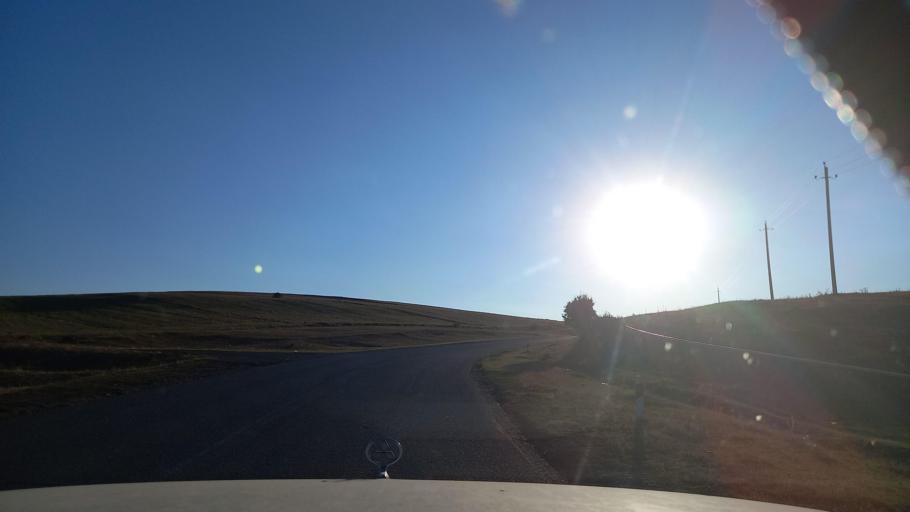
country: AZ
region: Shamkir Rayon
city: Shamkhor
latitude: 40.7660
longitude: 45.9519
